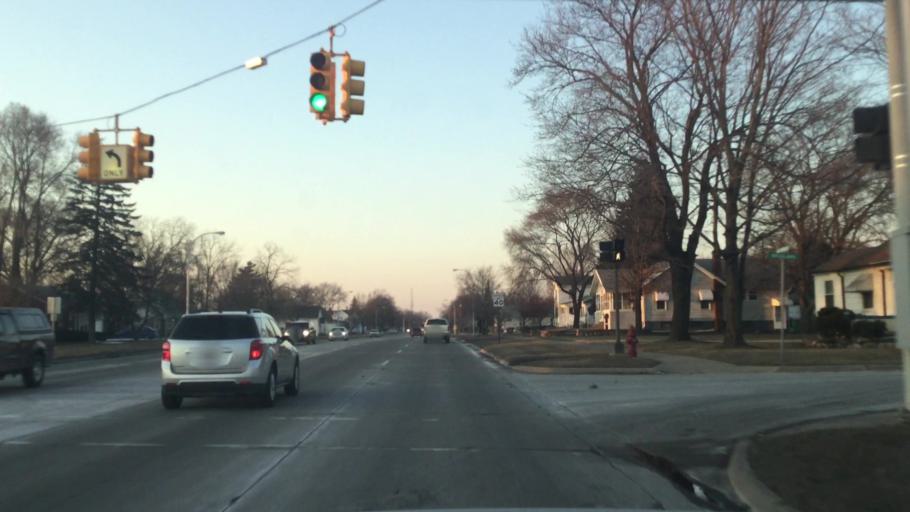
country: US
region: Michigan
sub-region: Wayne County
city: Garden City
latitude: 42.3278
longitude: -83.3505
